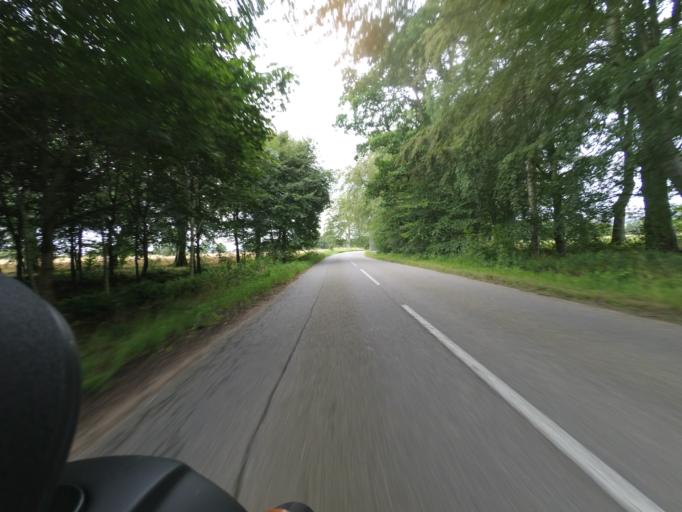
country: GB
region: Scotland
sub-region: Aberdeenshire
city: Laurencekirk
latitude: 56.8504
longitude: -2.5660
